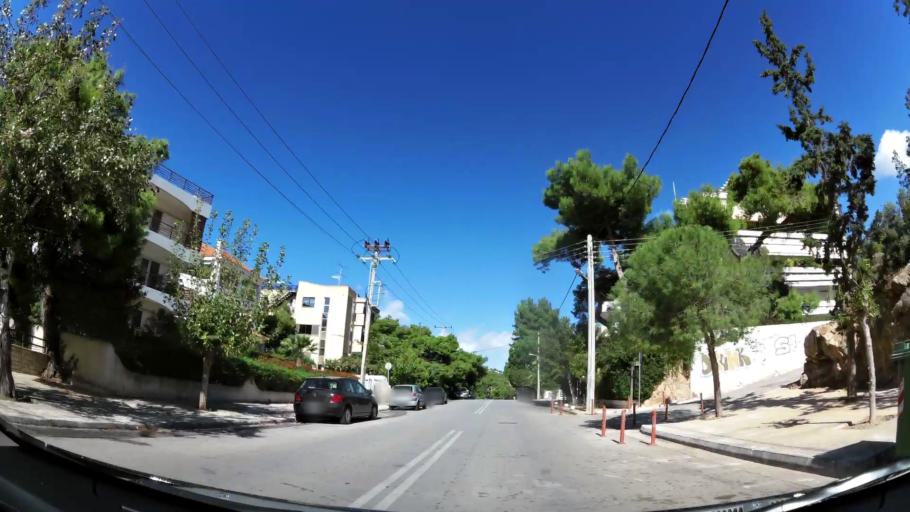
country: GR
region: Attica
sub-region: Nomarchia Anatolikis Attikis
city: Vouliagmeni
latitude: 37.8174
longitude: 23.7811
